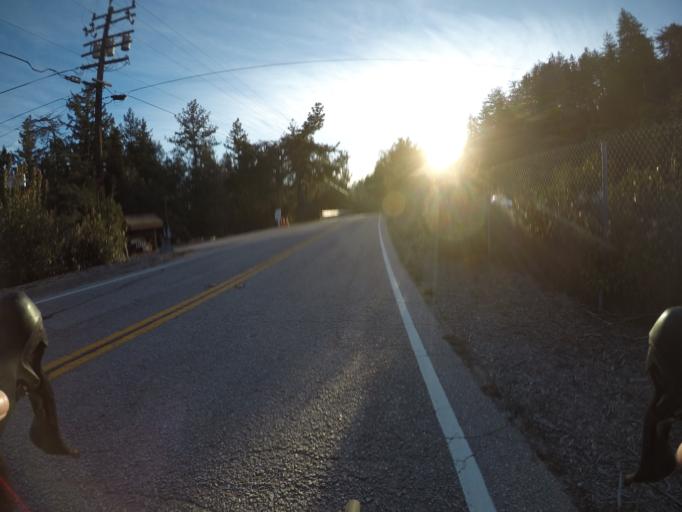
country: US
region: California
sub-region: Santa Cruz County
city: Pasatiempo
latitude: 37.0280
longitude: -122.0233
